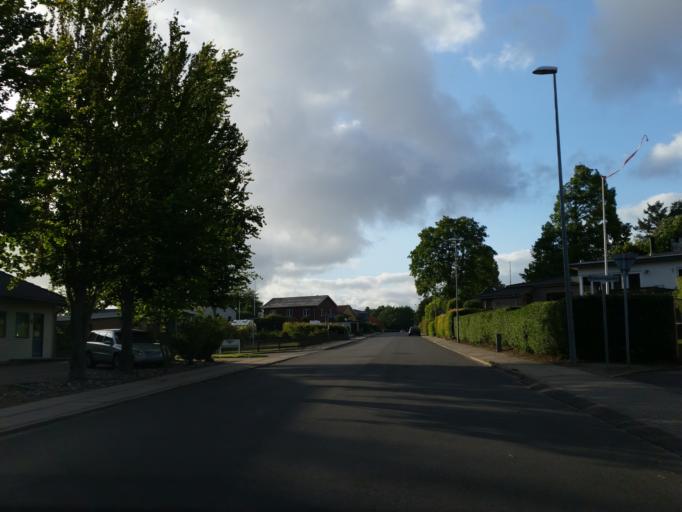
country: DK
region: South Denmark
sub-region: Vejle Kommune
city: Brejning
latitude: 55.6629
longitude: 9.6736
